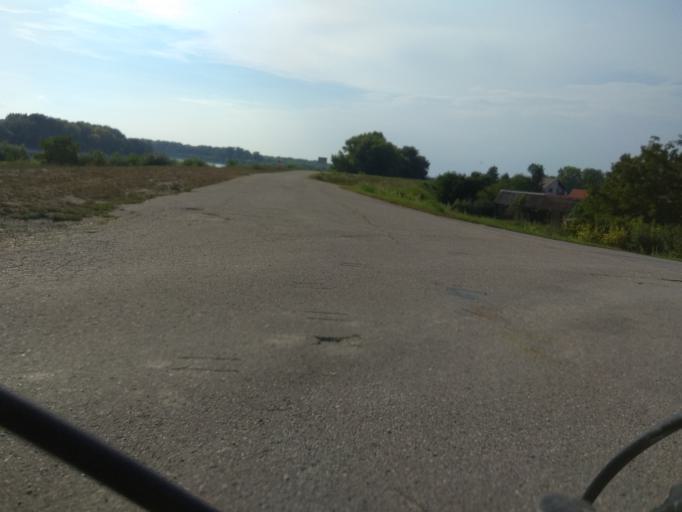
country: SK
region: Trnavsky
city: Gabcikovo
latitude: 47.8193
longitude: 17.6155
